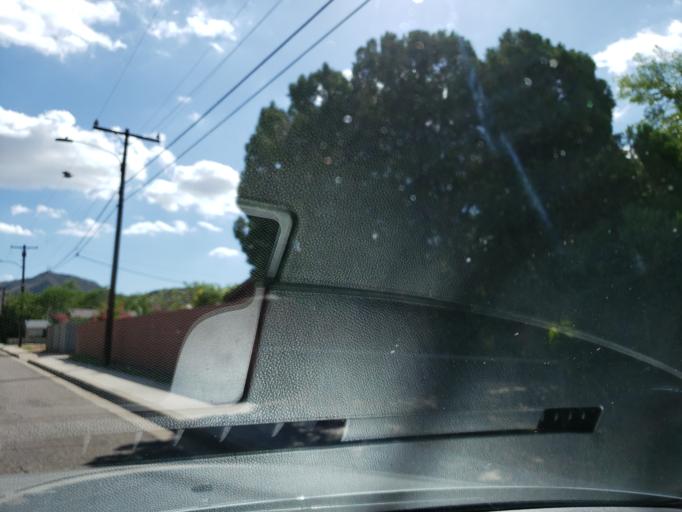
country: US
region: Arizona
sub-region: Maricopa County
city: Glendale
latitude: 33.5875
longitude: -112.0974
